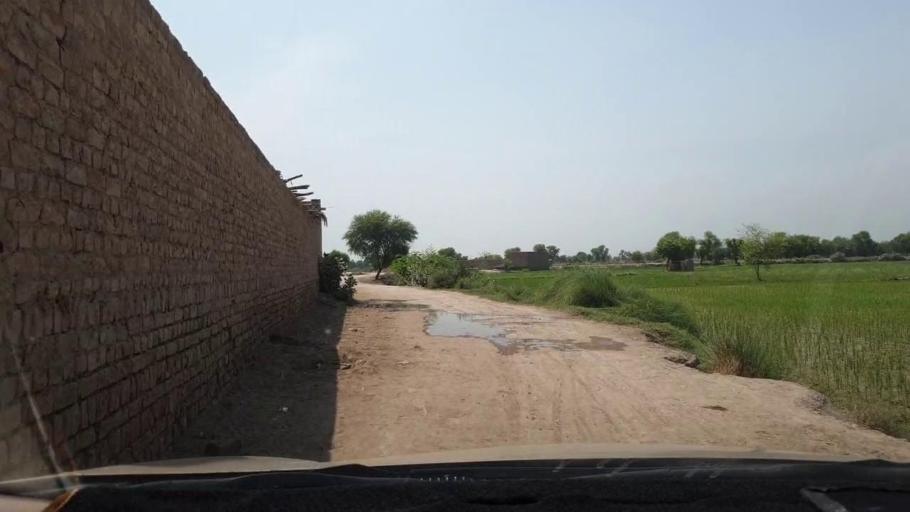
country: PK
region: Sindh
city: Naudero
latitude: 27.6466
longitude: 68.2742
